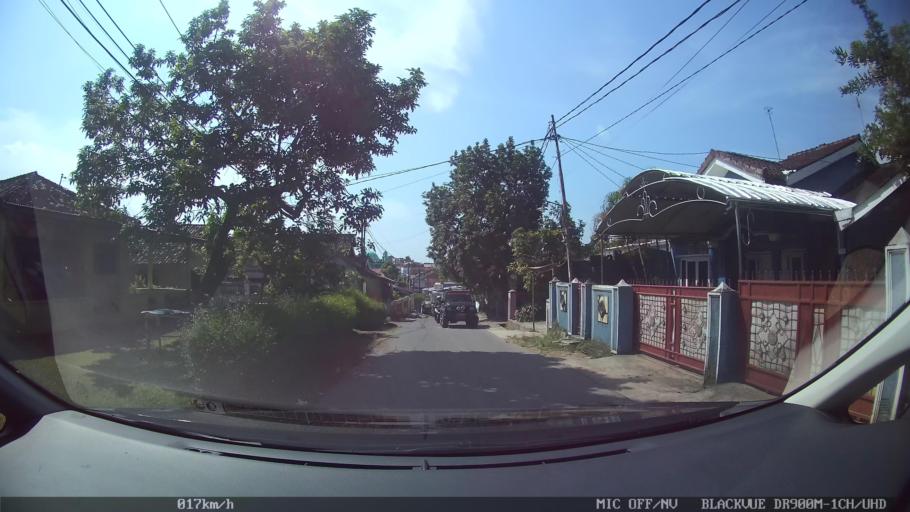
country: ID
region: Lampung
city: Kedaton
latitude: -5.3721
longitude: 105.2506
